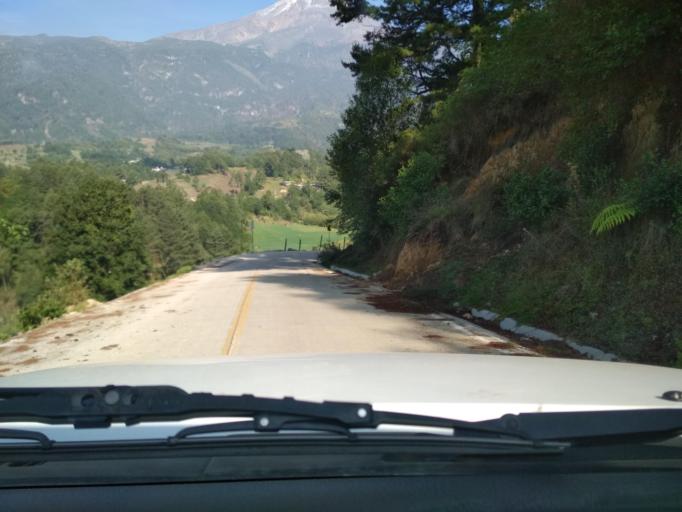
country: MX
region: Veracruz
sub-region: La Perla
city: Chilapa
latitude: 19.0026
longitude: -97.1774
